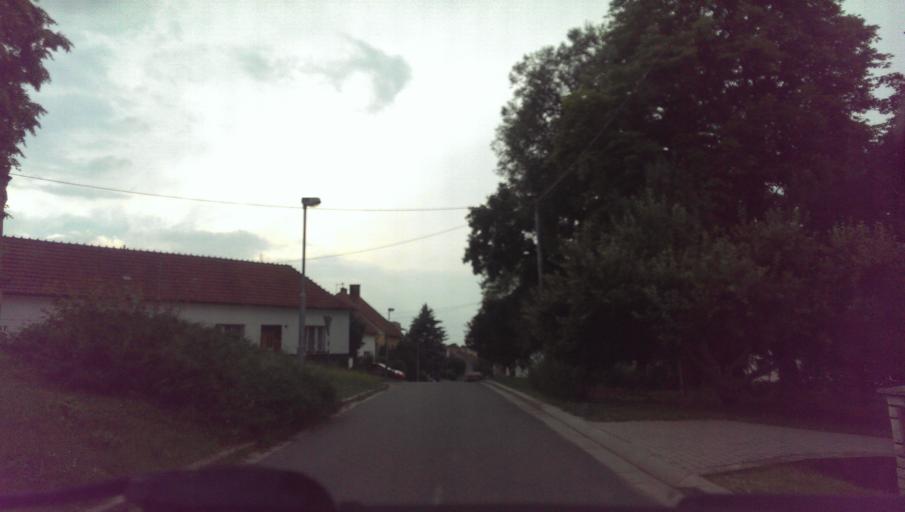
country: CZ
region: Zlin
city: Popovice
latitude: 49.0344
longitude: 17.5067
